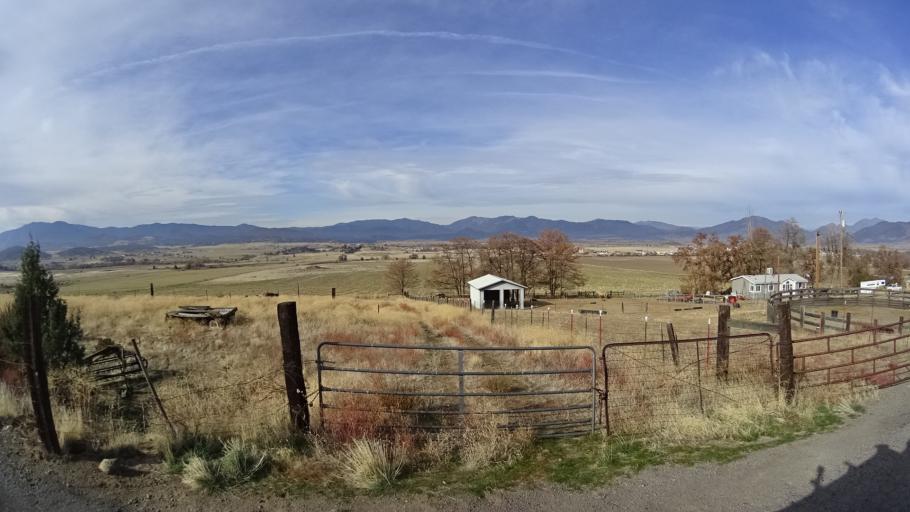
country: US
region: California
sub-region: Siskiyou County
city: Montague
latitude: 41.7148
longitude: -122.5216
